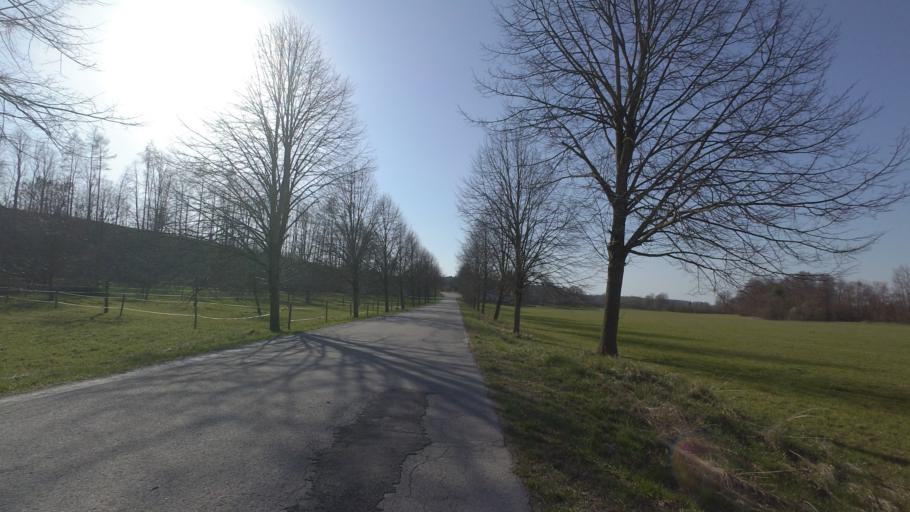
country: DE
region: Bavaria
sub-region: Upper Bavaria
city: Traunreut
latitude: 47.9405
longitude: 12.5907
